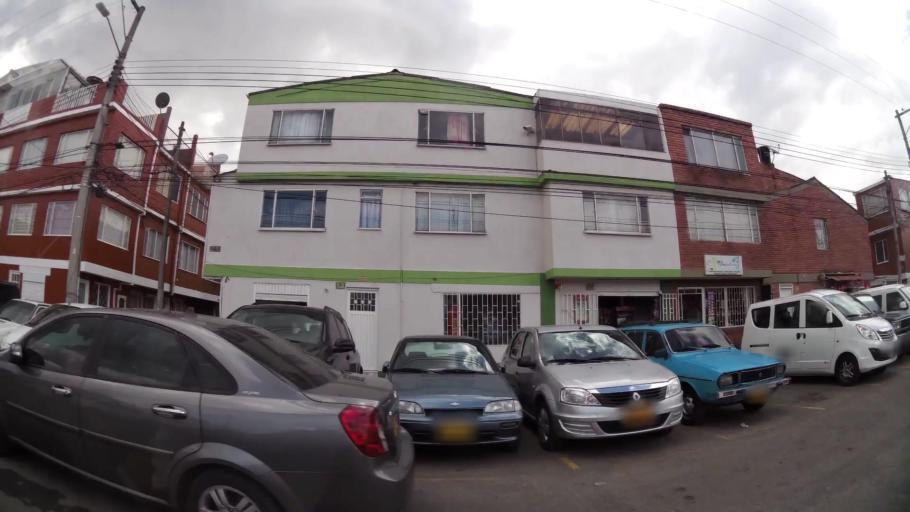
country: CO
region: Cundinamarca
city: Cota
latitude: 4.7387
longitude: -74.0984
